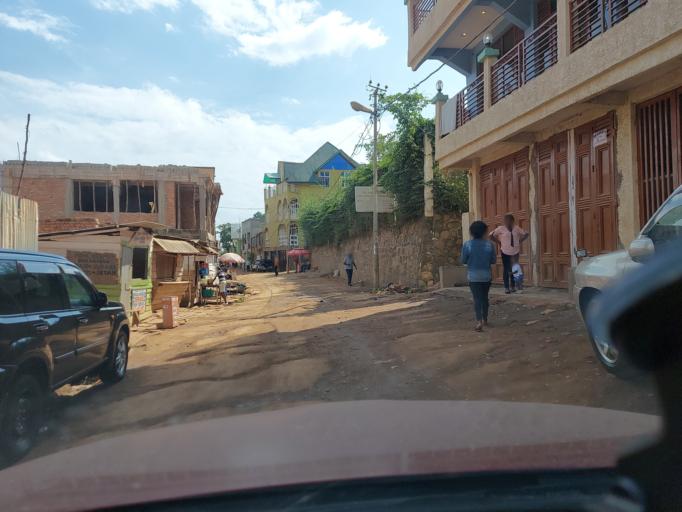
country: CD
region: South Kivu
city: Bukavu
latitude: -2.4975
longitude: 28.8584
